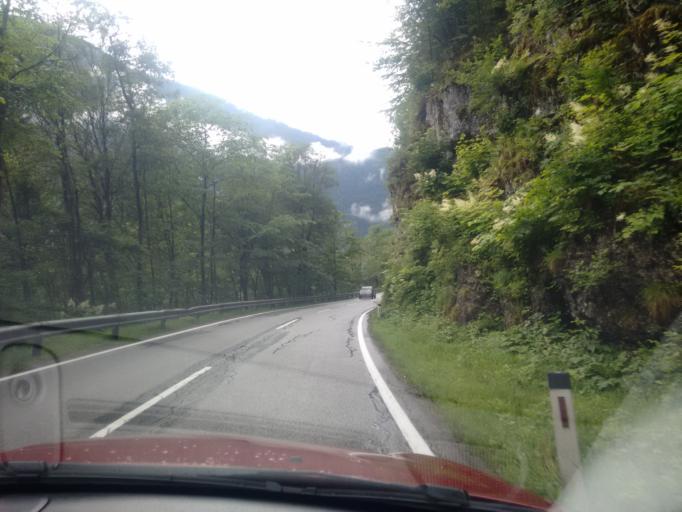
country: AT
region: Upper Austria
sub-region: Politischer Bezirk Gmunden
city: Bad Goisern
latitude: 47.5896
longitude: 13.6552
